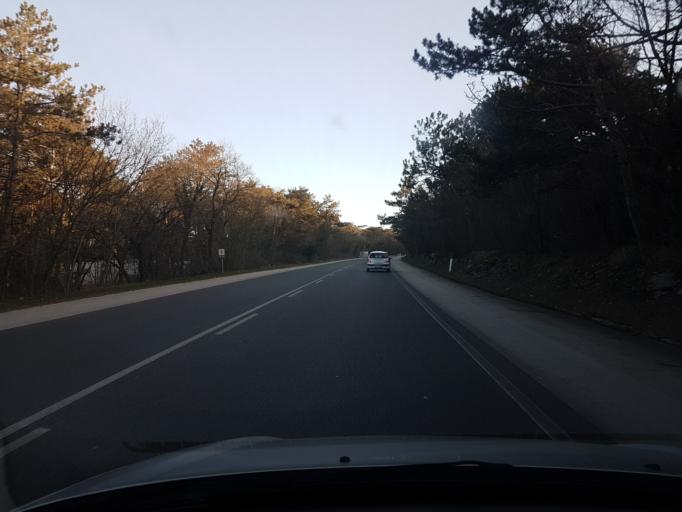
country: IT
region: Friuli Venezia Giulia
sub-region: Provincia di Trieste
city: Villa Opicina
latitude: 45.6967
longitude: 13.7635
